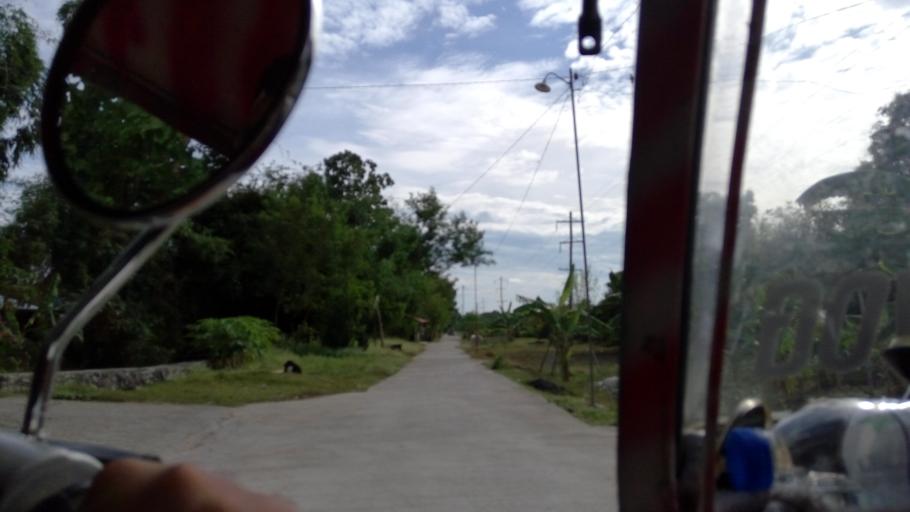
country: PH
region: Ilocos
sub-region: Province of La Union
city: San Eugenio
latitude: 16.3705
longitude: 120.3523
